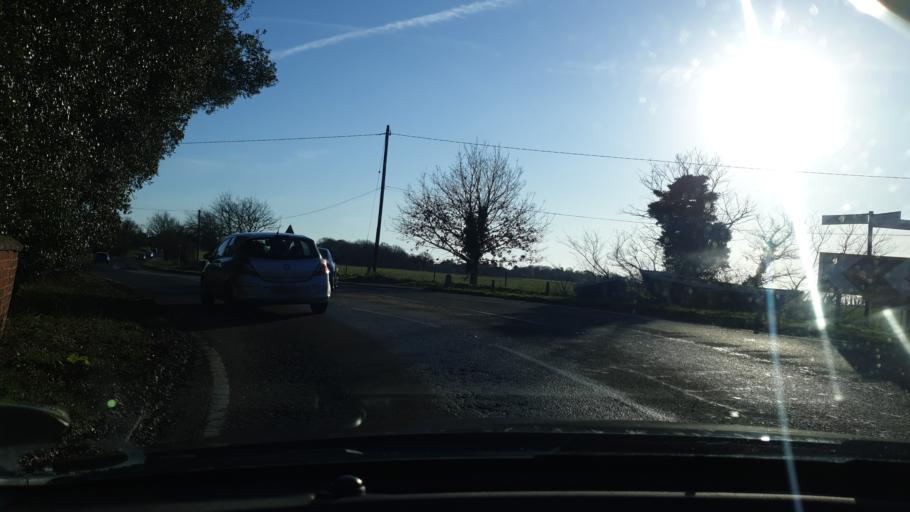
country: GB
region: England
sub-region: Essex
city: Brightlingsea
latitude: 51.8283
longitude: 1.0137
